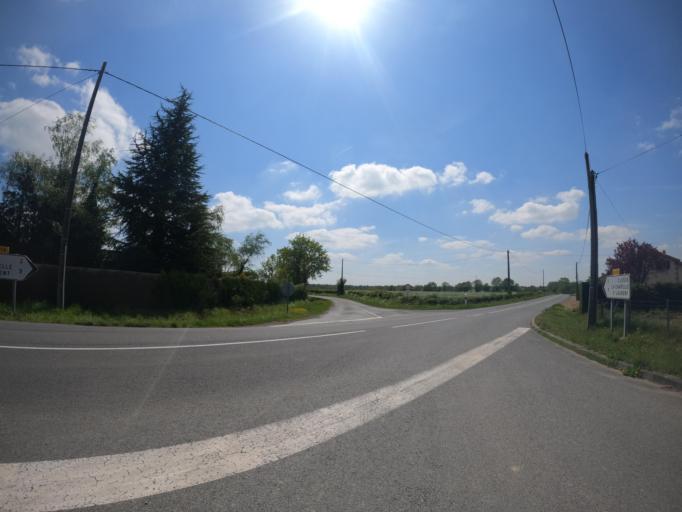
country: FR
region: Poitou-Charentes
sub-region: Departement des Deux-Sevres
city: Boisme
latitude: 46.7237
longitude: -0.3825
